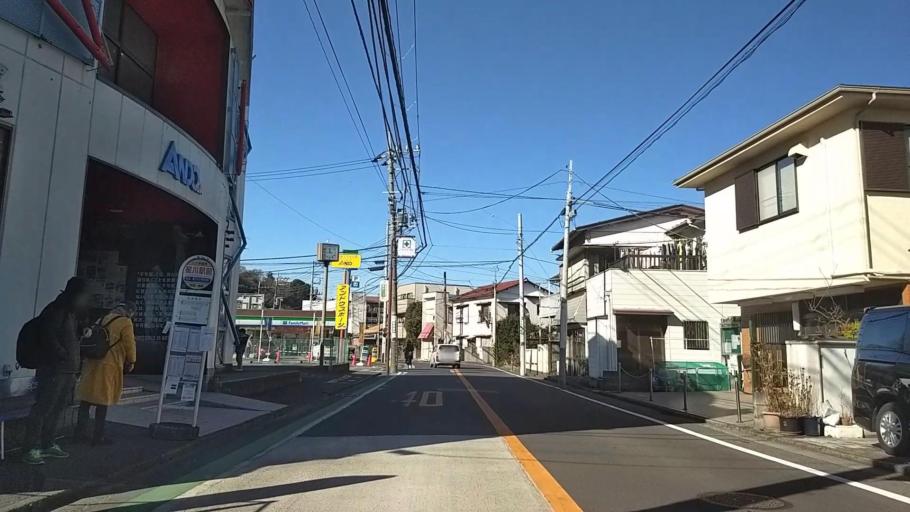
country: JP
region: Kanagawa
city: Yokohama
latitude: 35.4582
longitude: 139.5932
